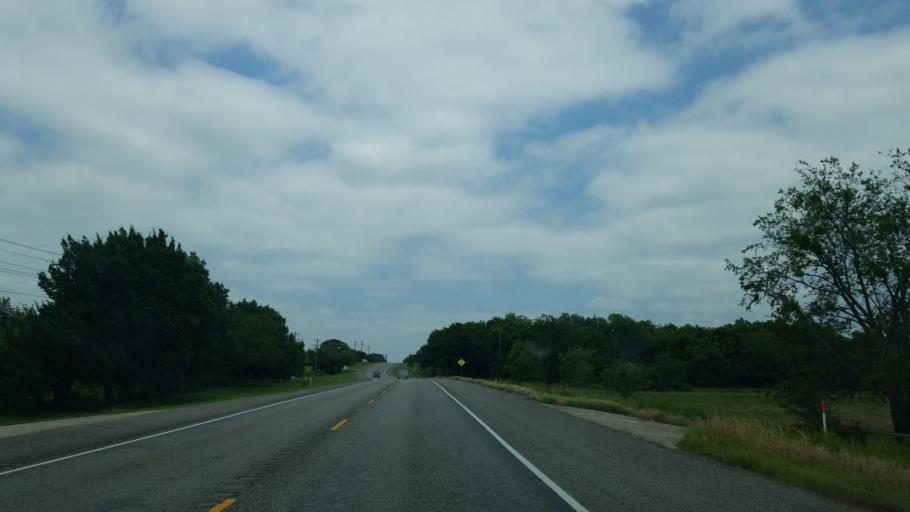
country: US
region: Texas
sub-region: Denton County
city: Aubrey
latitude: 33.3055
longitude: -97.0304
